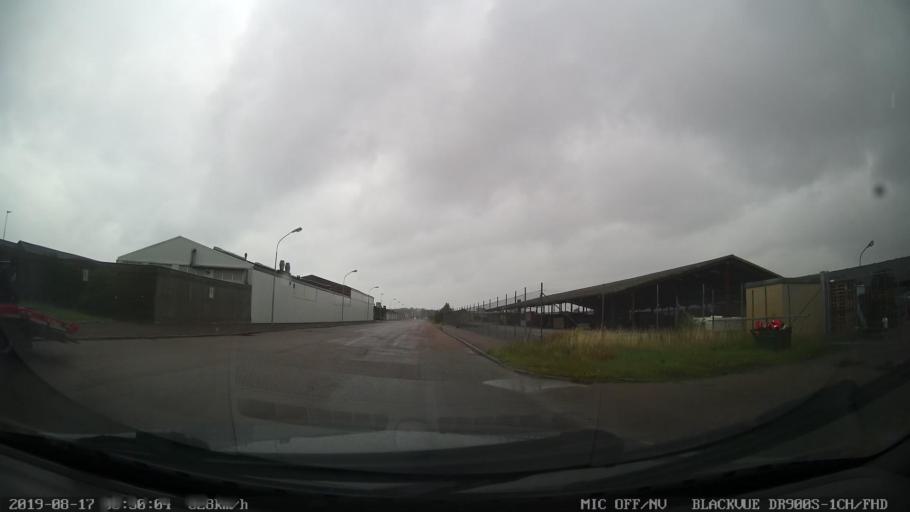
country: SE
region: Skane
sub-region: Landskrona
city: Landskrona
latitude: 55.8646
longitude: 12.8455
